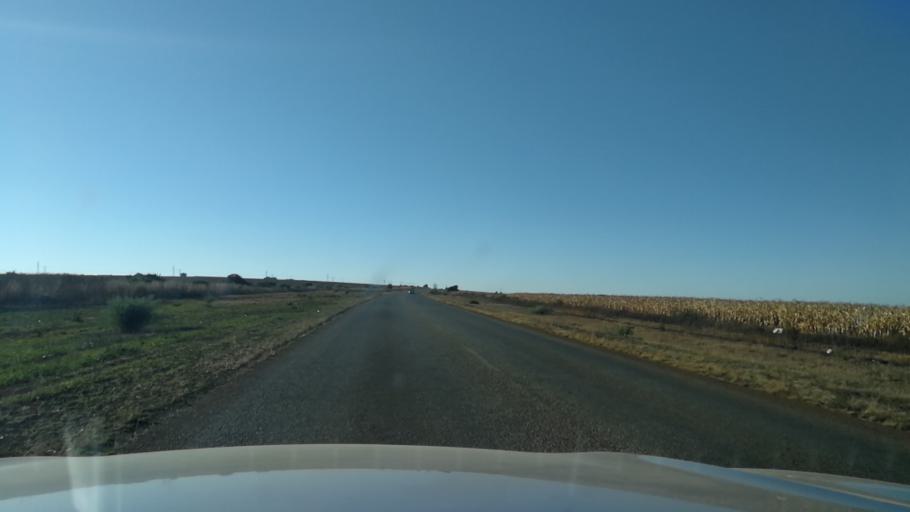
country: ZA
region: North-West
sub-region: Bojanala Platinum District Municipality
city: Rustenburg
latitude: -25.9852
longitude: 27.2739
